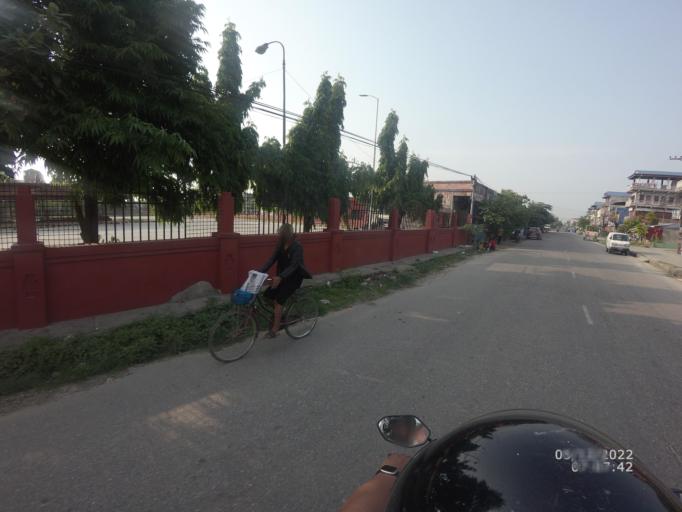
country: NP
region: Central Region
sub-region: Narayani Zone
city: Bharatpur
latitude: 27.6679
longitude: 84.4383
